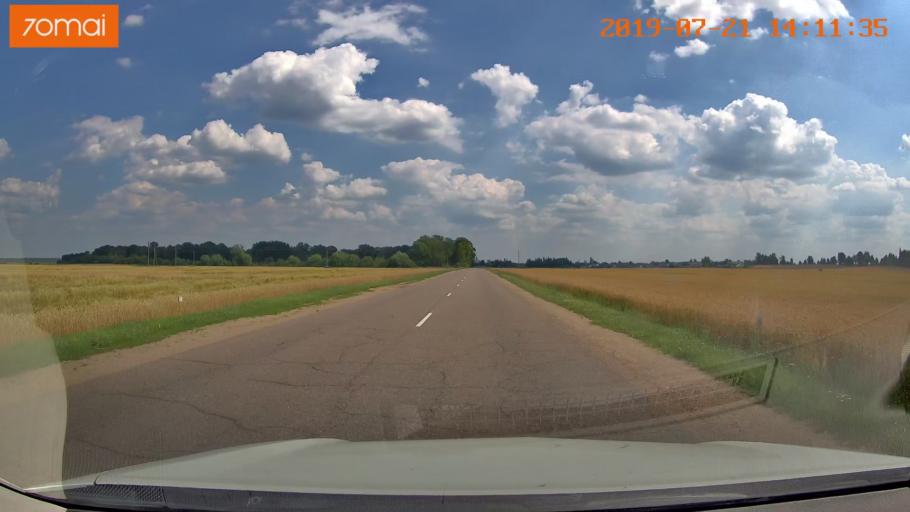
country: BY
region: Grodnenskaya
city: Karelichy
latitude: 53.6566
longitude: 26.1555
